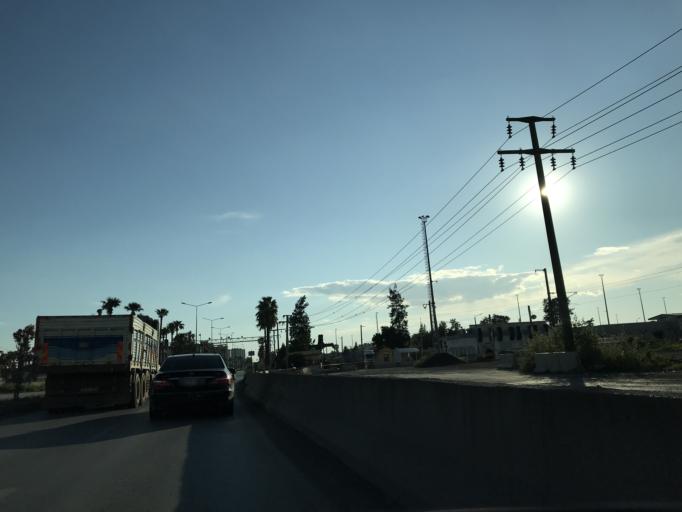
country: TR
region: Hatay
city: Iskenderun
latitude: 36.5910
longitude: 36.1923
